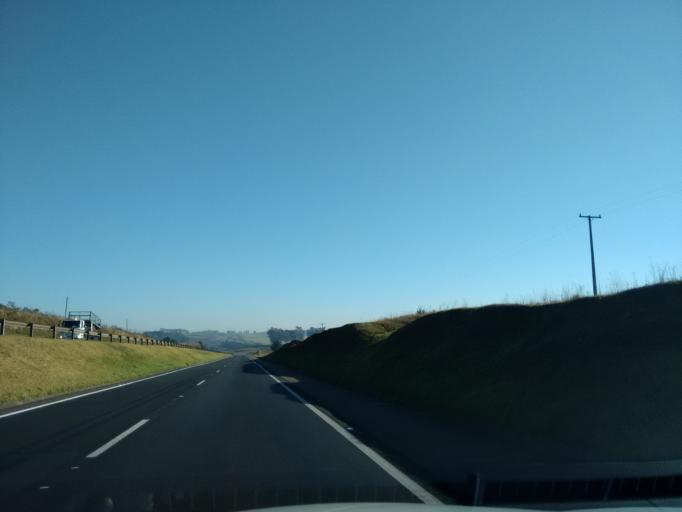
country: BR
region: Parana
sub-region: Campo Largo
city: Campo Largo
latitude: -25.4486
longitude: -49.7400
